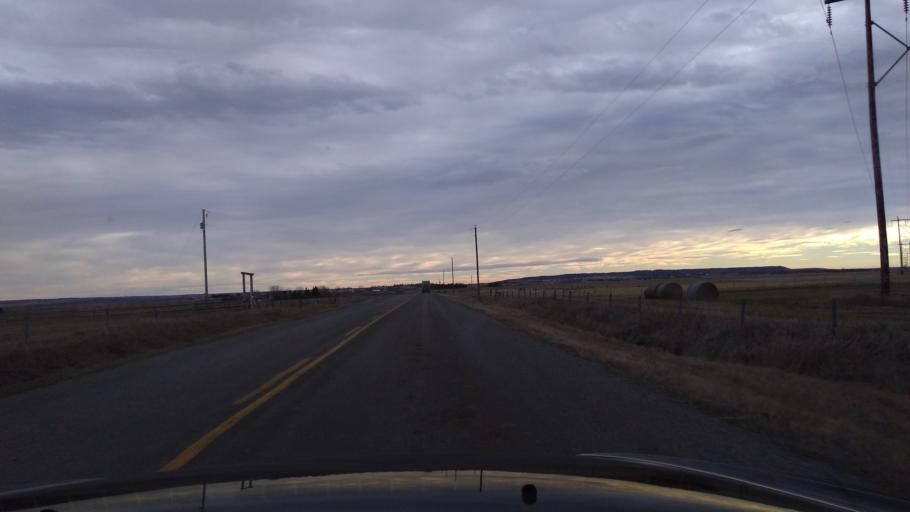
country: CA
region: Alberta
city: Cochrane
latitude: 51.0960
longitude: -114.4098
